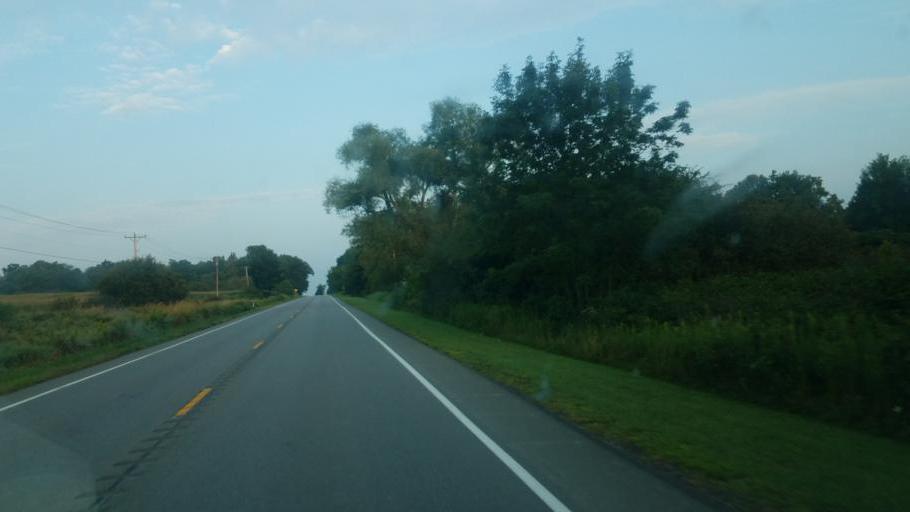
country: US
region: Pennsylvania
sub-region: Crawford County
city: Conneaut Lakeshore
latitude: 41.6051
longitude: -80.3440
